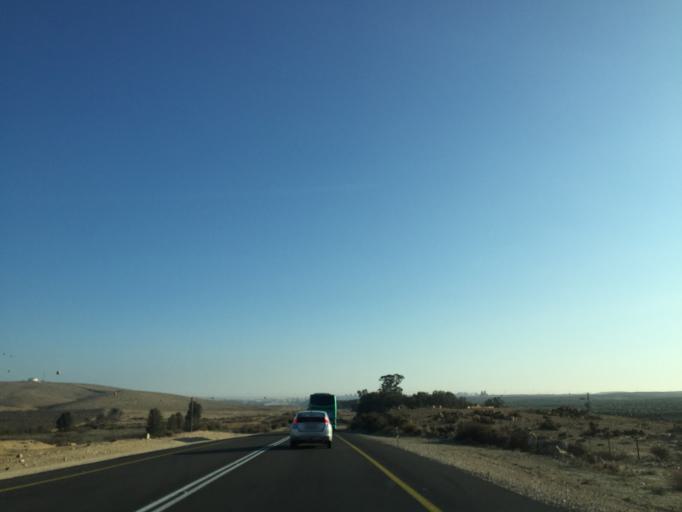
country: IL
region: Southern District
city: Dimona
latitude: 31.0469
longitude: 34.9842
